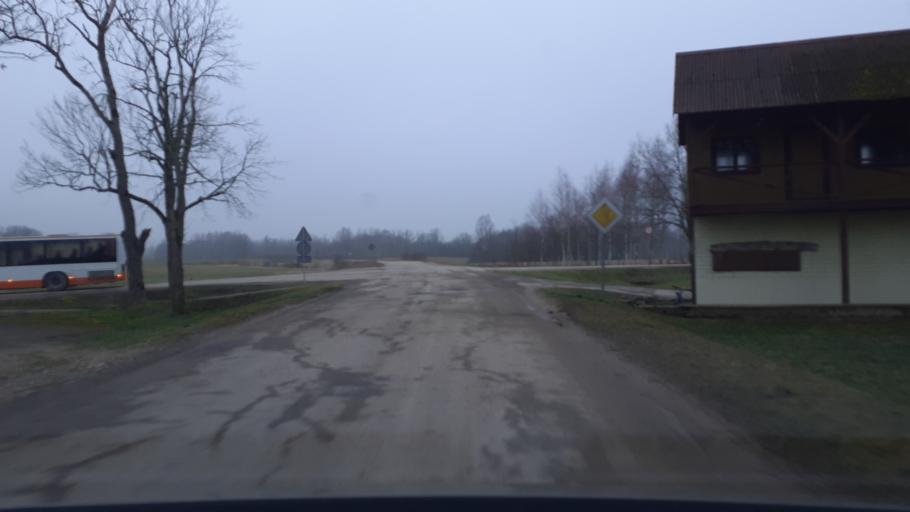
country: LV
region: Talsu Rajons
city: Sabile
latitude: 56.9556
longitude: 22.3944
